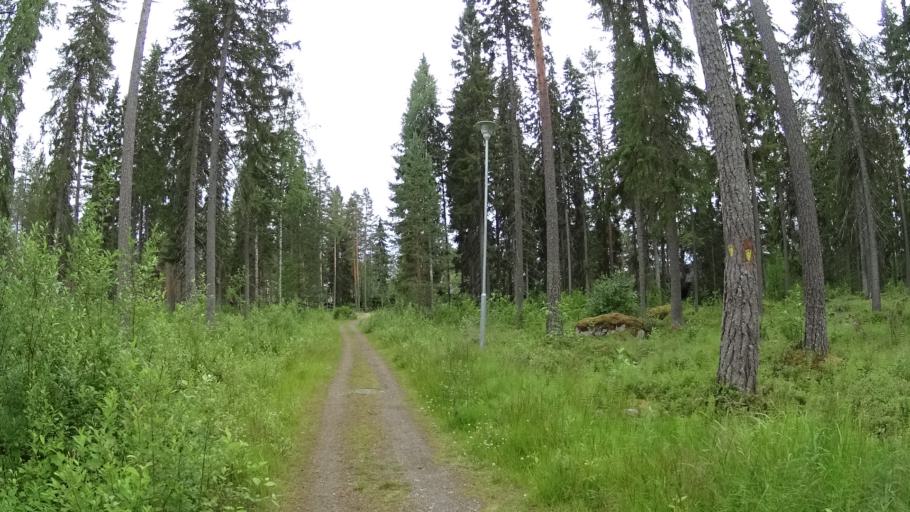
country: FI
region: Southern Ostrobothnia
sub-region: Kuusiokunnat
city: AEhtaeri
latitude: 62.5291
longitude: 24.1934
